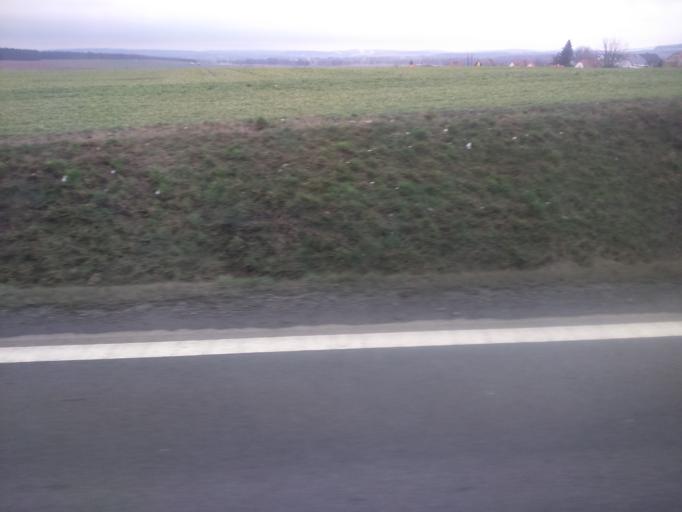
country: CZ
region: Plzensky
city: Chotesov
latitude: 49.6624
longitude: 13.2030
